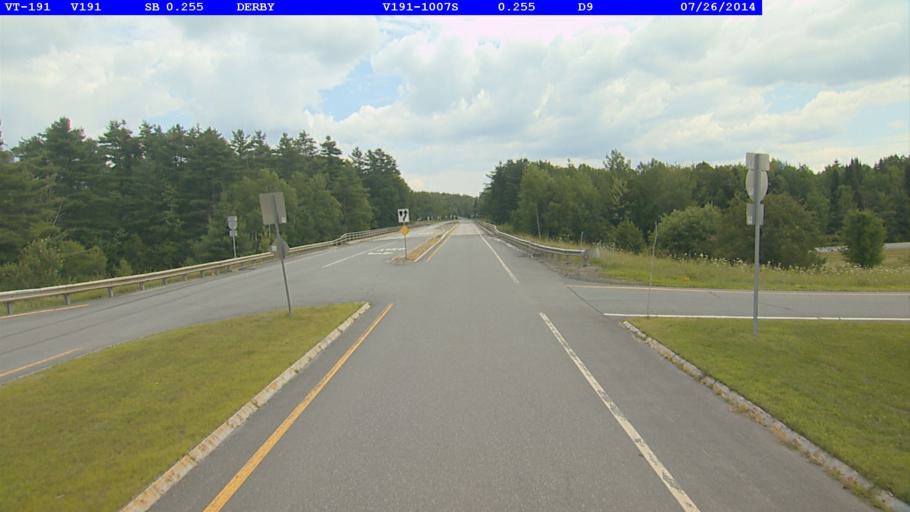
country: US
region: Vermont
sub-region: Orleans County
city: Newport
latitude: 44.9234
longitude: -72.1744
